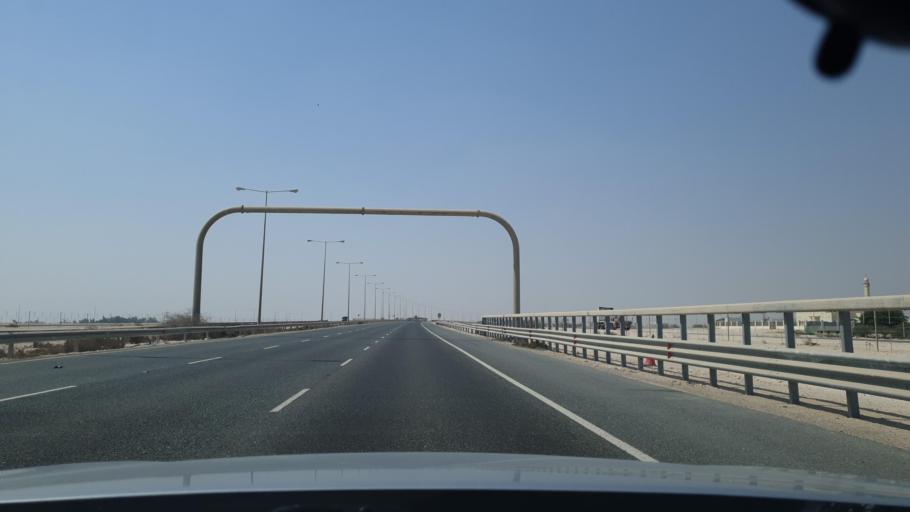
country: QA
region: Al Khawr
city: Al Khawr
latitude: 25.7542
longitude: 51.4445
